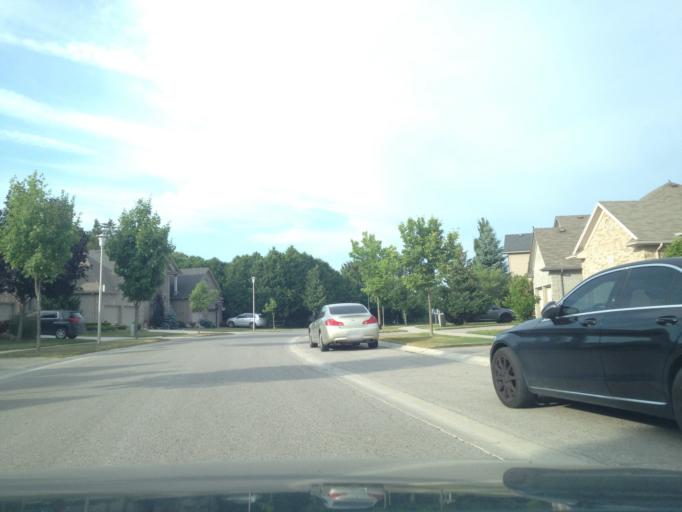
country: CA
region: Ontario
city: London
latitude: 43.0397
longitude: -81.2789
